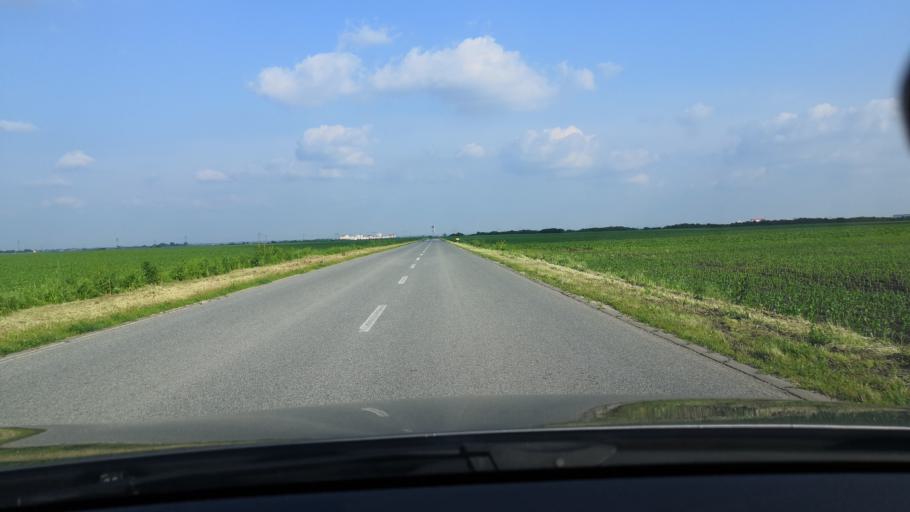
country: RS
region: Autonomna Pokrajina Vojvodina
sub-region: Sremski Okrug
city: Ingija
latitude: 45.0812
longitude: 20.1172
